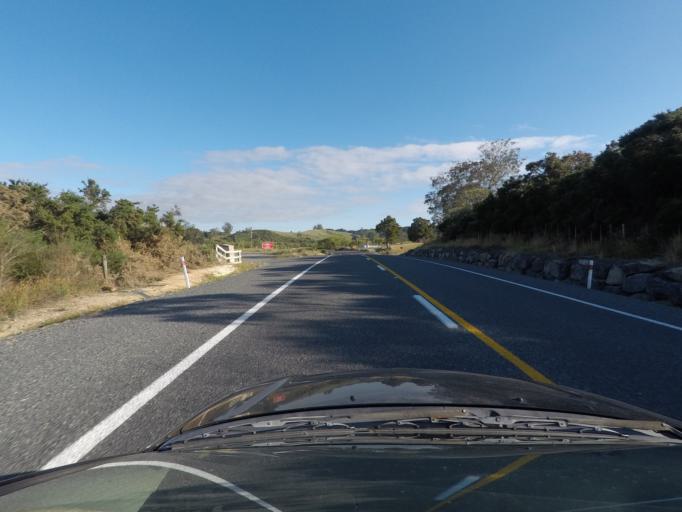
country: NZ
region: Northland
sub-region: Far North District
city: Kawakawa
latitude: -35.4132
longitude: 174.0731
